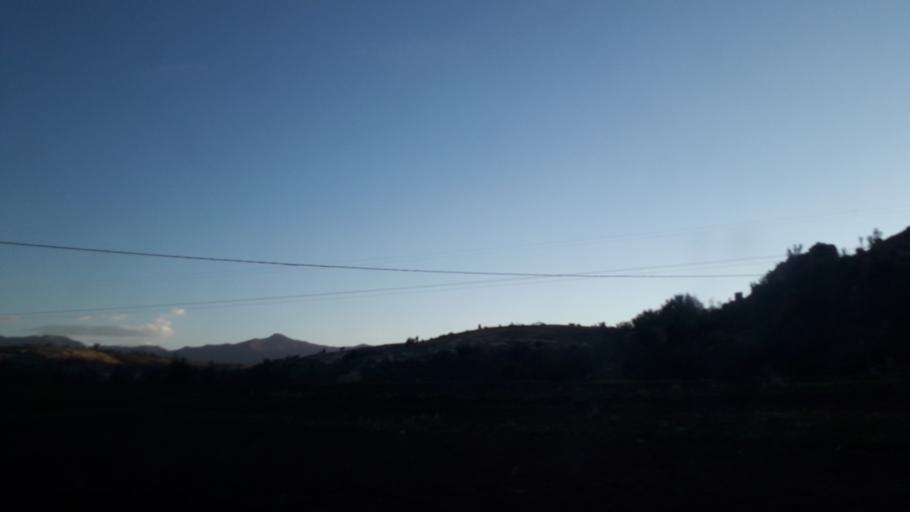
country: LS
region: Butha-Buthe
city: Butha-Buthe
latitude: -28.7311
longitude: 28.3980
